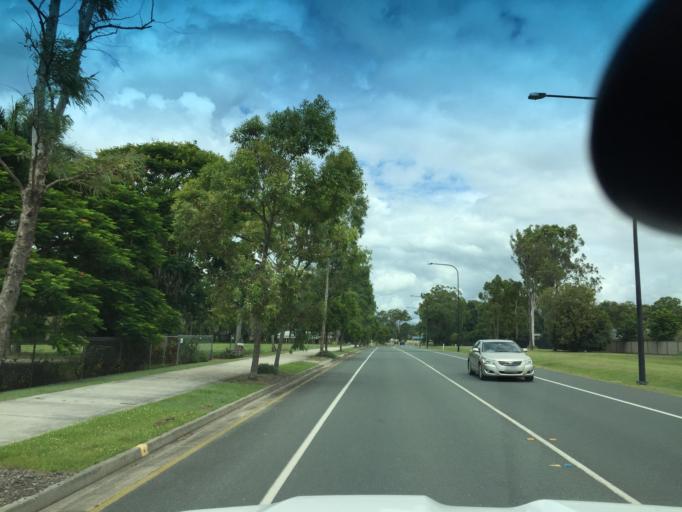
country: AU
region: Queensland
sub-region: Moreton Bay
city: Burpengary
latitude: -27.1266
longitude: 152.9909
